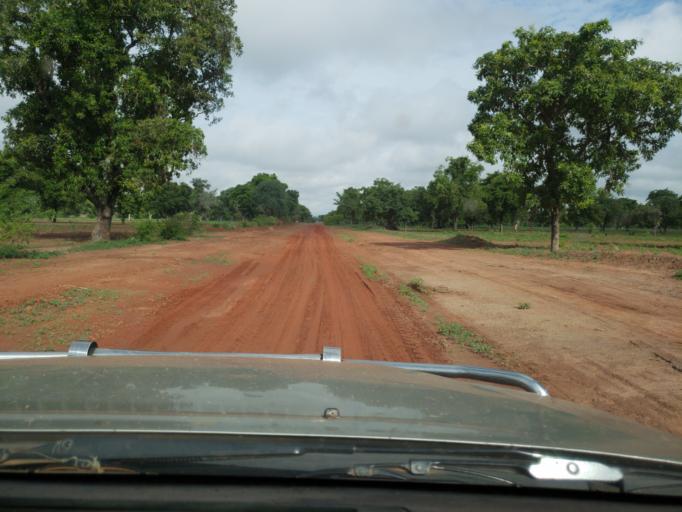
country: ML
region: Sikasso
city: Koutiala
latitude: 12.3925
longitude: -6.0131
